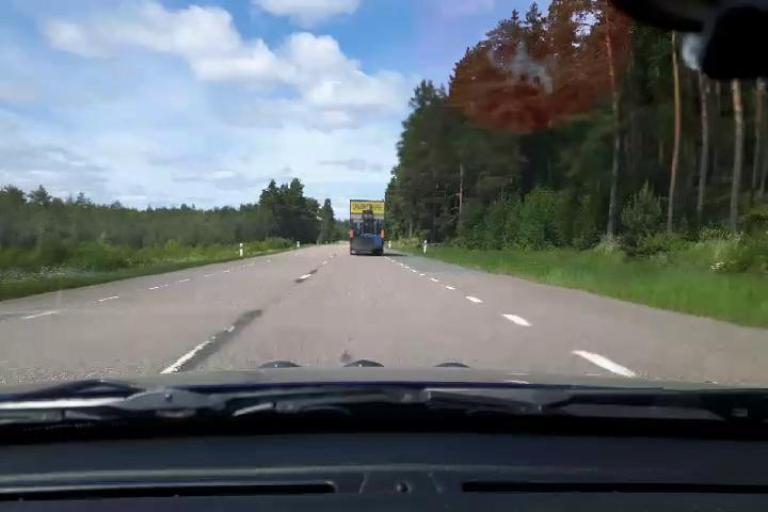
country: SE
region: Uppsala
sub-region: Osthammars Kommun
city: Bjorklinge
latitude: 60.1014
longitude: 17.5520
